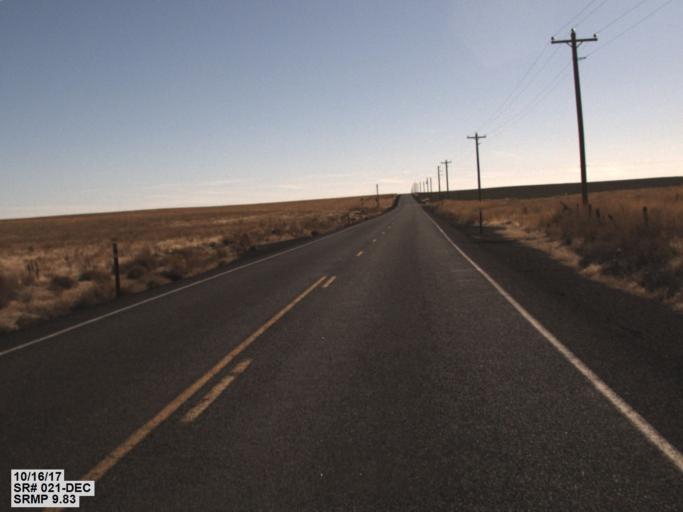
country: US
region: Washington
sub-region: Franklin County
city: Connell
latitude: 46.7685
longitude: -118.5475
